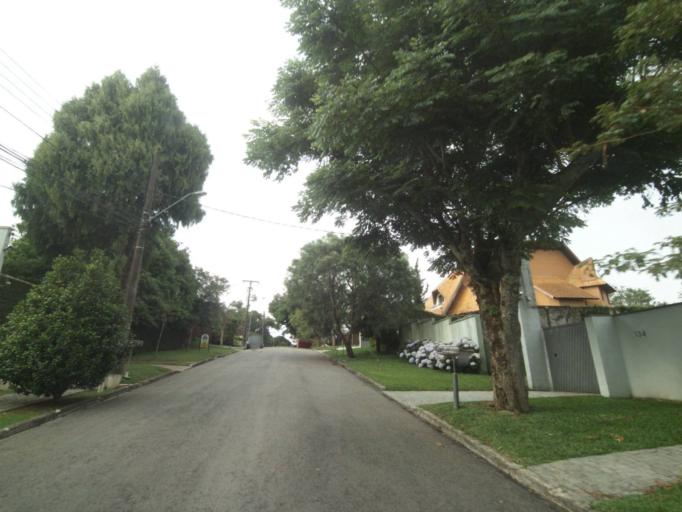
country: BR
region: Parana
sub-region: Curitiba
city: Curitiba
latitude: -25.4088
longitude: -49.3116
